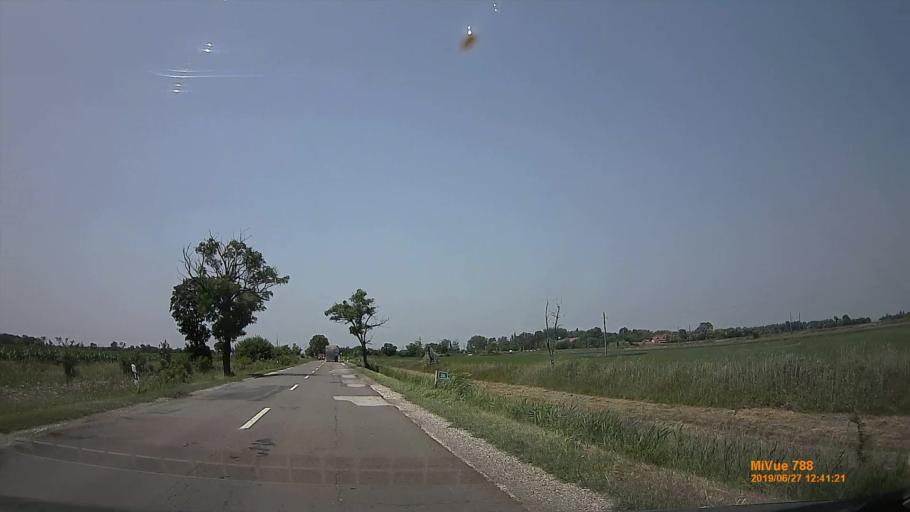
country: HU
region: Pest
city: Tortel
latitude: 47.1803
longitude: 19.8983
